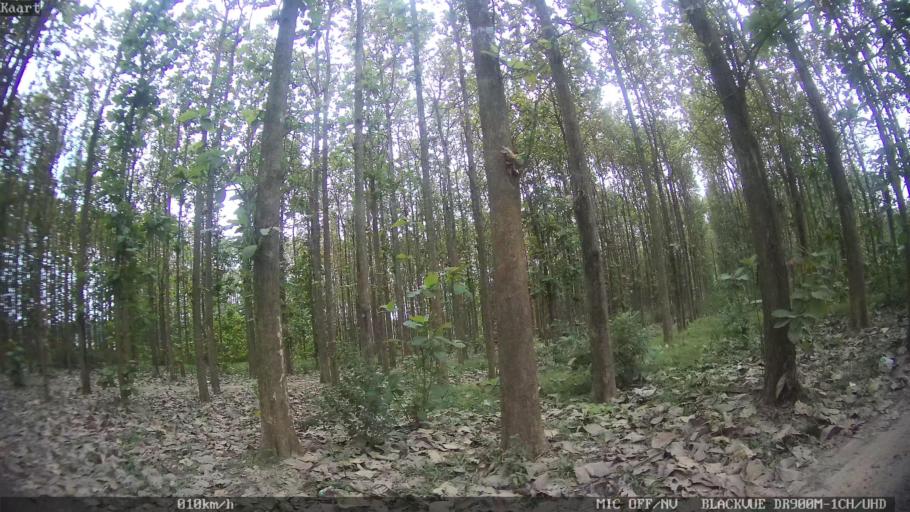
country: ID
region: Lampung
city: Panjang
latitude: -5.4074
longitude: 105.3574
